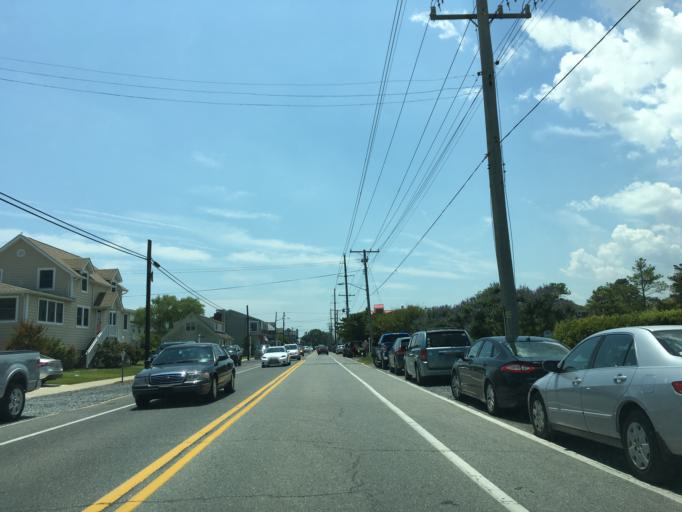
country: US
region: Delaware
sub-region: Sussex County
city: Bethany Beach
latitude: 38.5417
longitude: -75.0576
